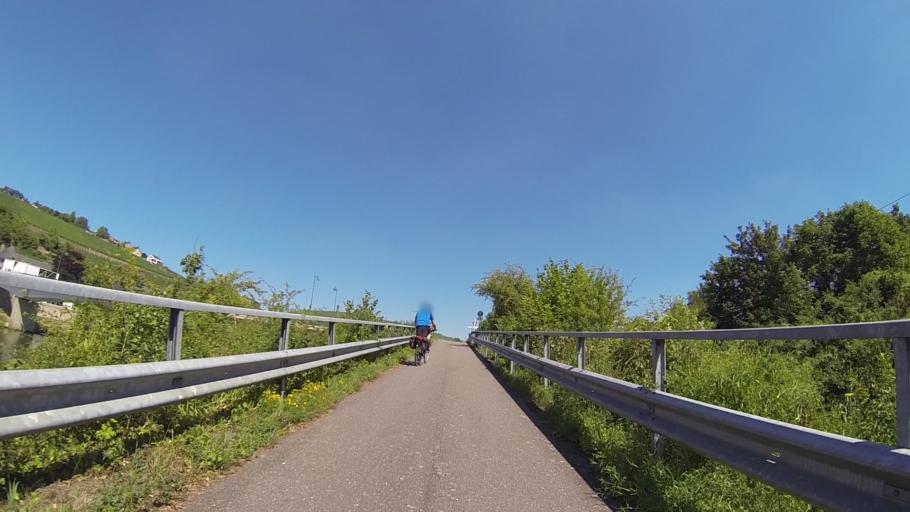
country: LU
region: Grevenmacher
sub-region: Canton de Grevenmacher
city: Wormeldange
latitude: 49.6064
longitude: 6.4045
